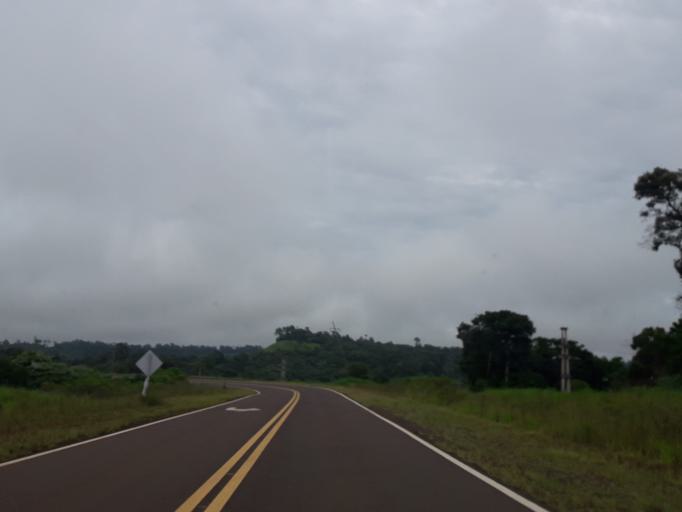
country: AR
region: Misiones
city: Bernardo de Irigoyen
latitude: -26.3925
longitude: -53.8051
